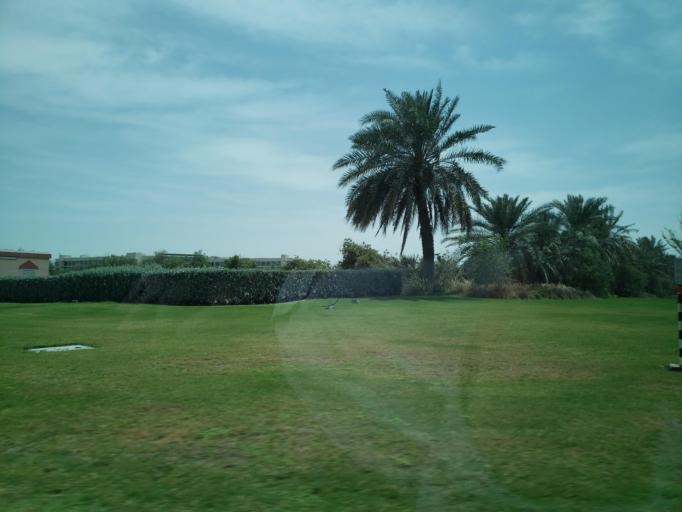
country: AE
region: Ash Shariqah
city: Sharjah
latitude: 25.3226
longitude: 55.5135
